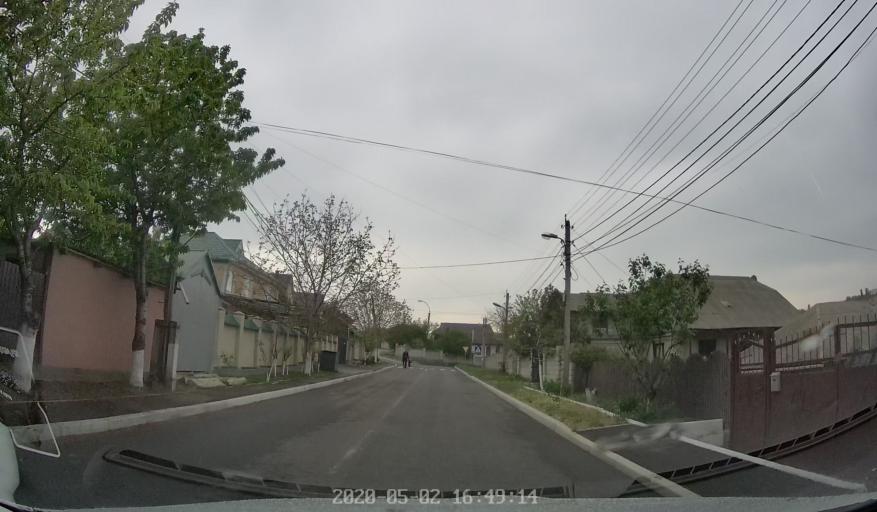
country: MD
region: Chisinau
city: Chisinau
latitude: 46.9688
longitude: 28.8284
